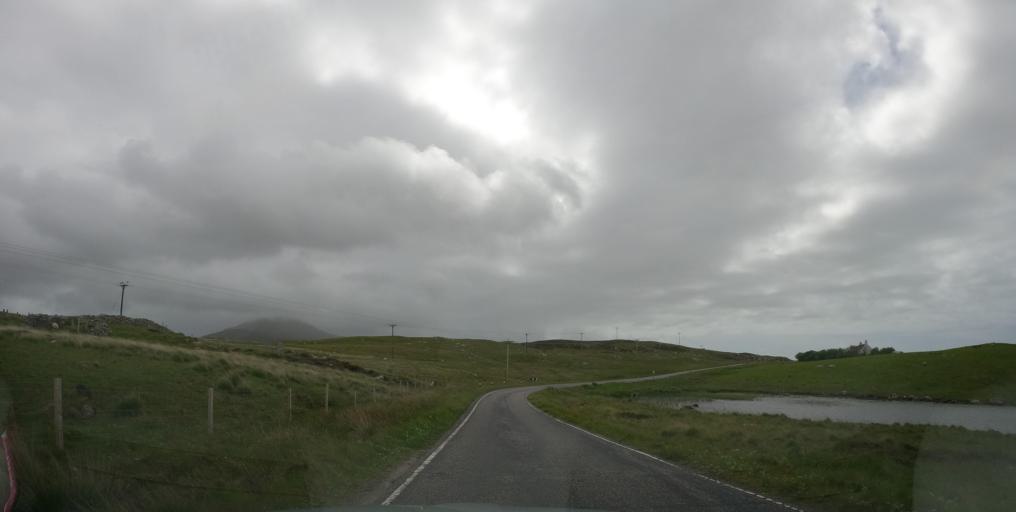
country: GB
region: Scotland
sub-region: Eilean Siar
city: Isle of South Uist
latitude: 57.2952
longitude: -7.3640
